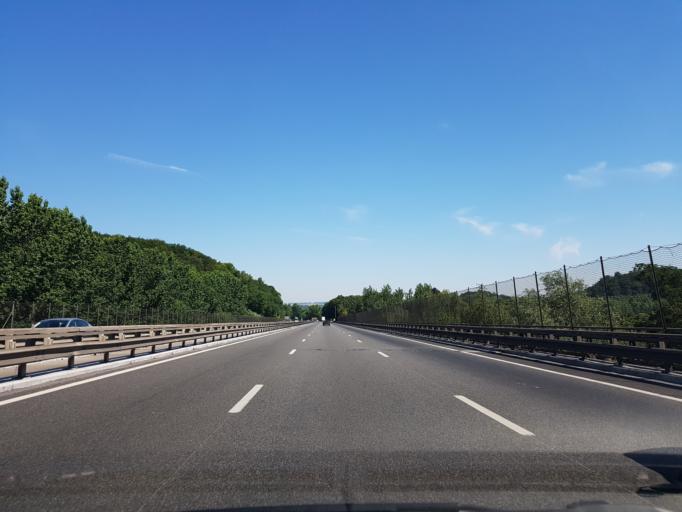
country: FR
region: Picardie
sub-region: Departement de l'Oise
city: Pontpoint
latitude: 49.2948
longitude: 2.6906
